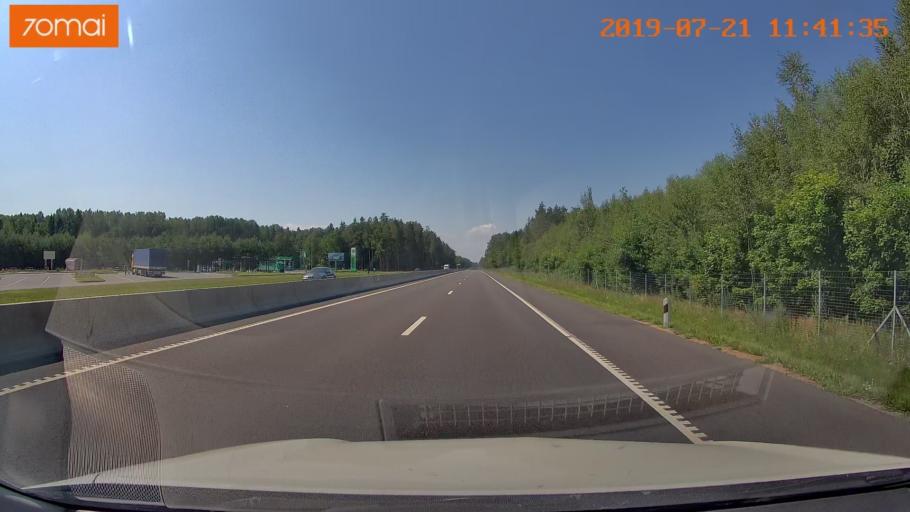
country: BY
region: Grodnenskaya
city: Lyubcha
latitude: 53.9443
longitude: 26.1476
